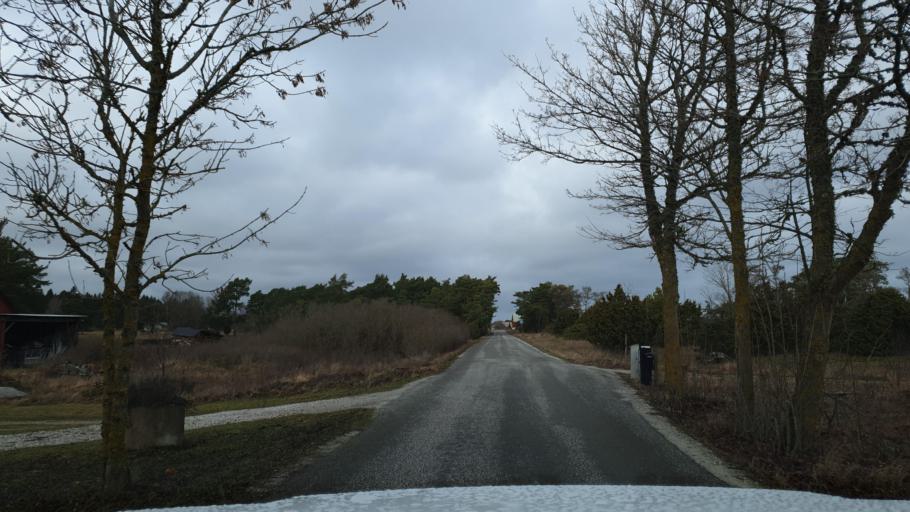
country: SE
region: Gotland
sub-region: Gotland
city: Slite
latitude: 57.3914
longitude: 18.8089
